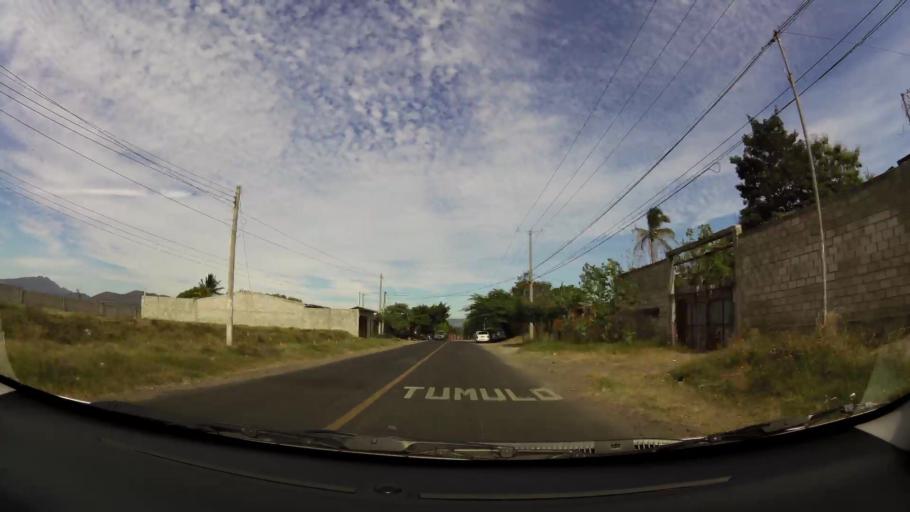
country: SV
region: Santa Ana
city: Chalchuapa
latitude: 13.9806
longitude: -89.6852
